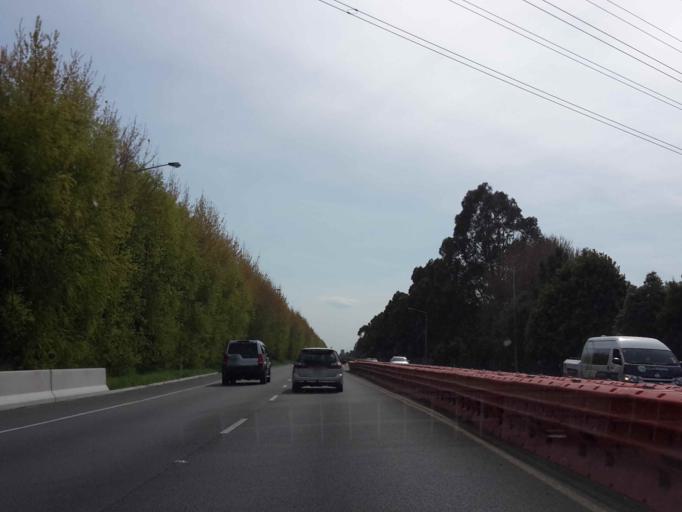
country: NZ
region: Canterbury
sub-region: Selwyn District
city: Prebbleton
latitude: -43.5120
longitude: 172.5389
